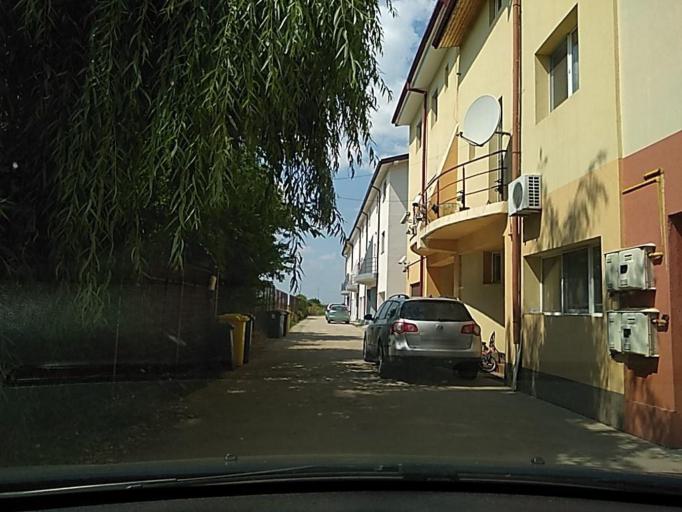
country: RO
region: Ilfov
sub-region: Comuna Domnesti
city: Domnesti
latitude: 44.4077
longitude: 25.9268
